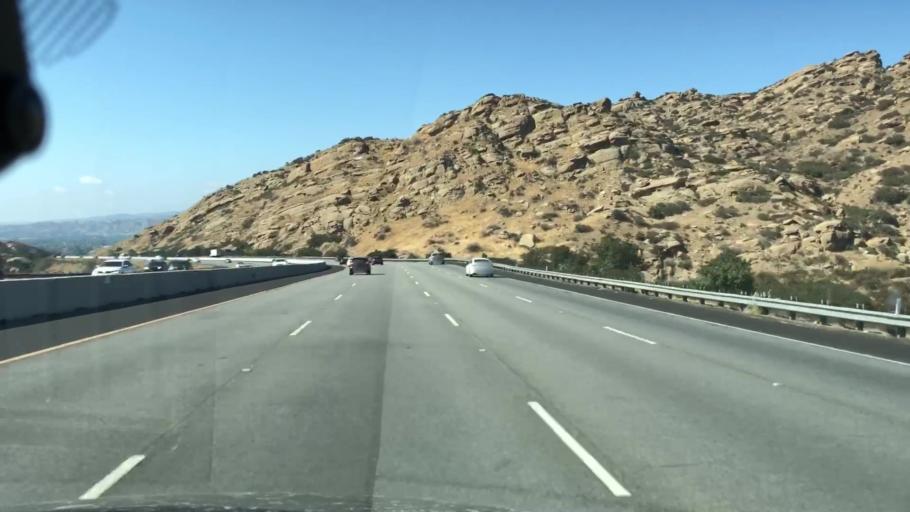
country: US
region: California
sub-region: Los Angeles County
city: Chatsworth
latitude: 34.2684
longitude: -118.6451
